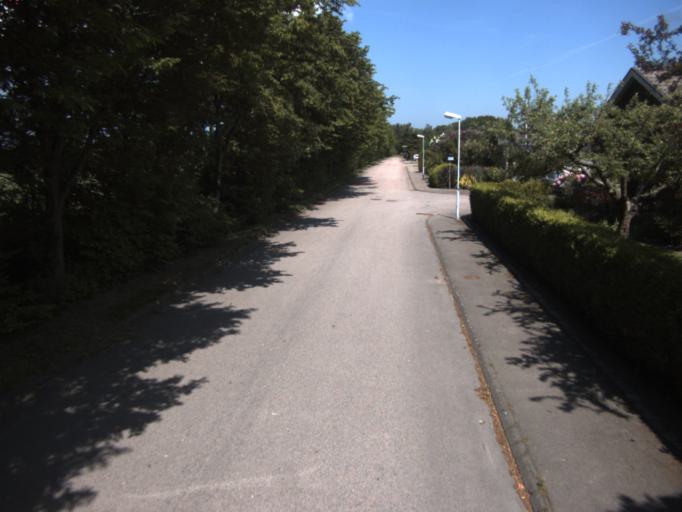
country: SE
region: Skane
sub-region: Helsingborg
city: Barslov
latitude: 56.0327
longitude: 12.8093
